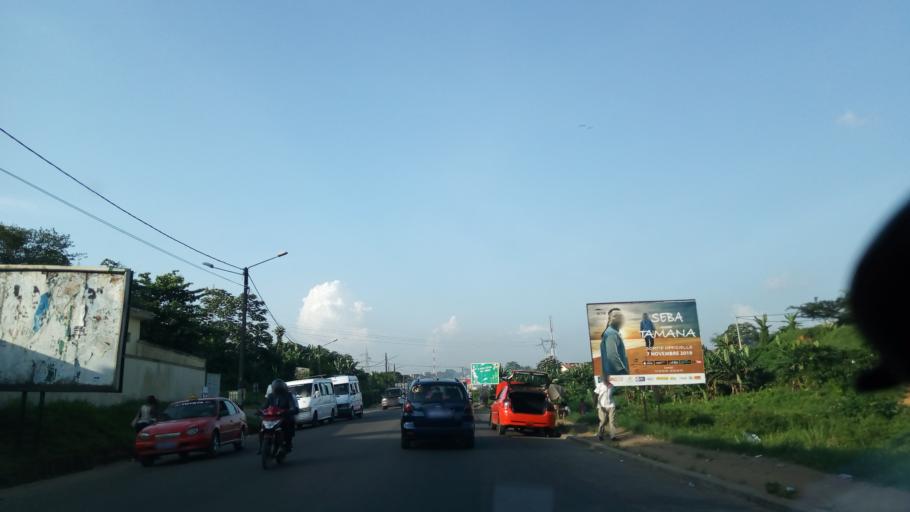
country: CI
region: Lagunes
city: Abobo
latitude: 5.3825
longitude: -4.0064
